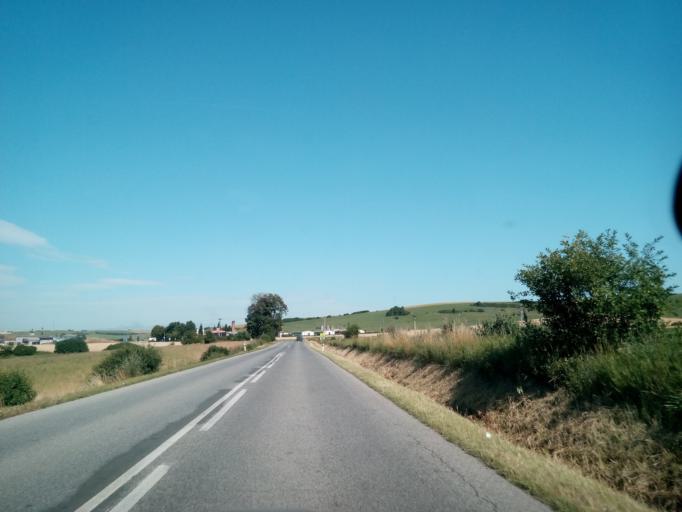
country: SK
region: Kosicky
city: Krompachy
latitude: 48.9438
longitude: 20.8153
